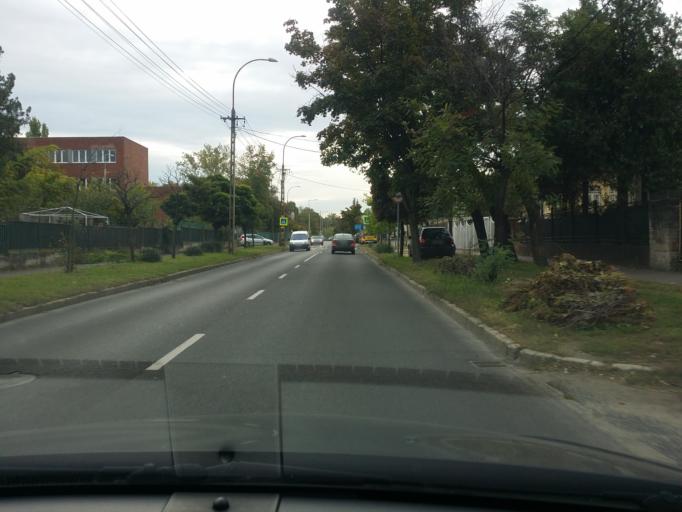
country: HU
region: Budapest
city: Budapest XV. keruelet
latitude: 47.5413
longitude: 19.1184
